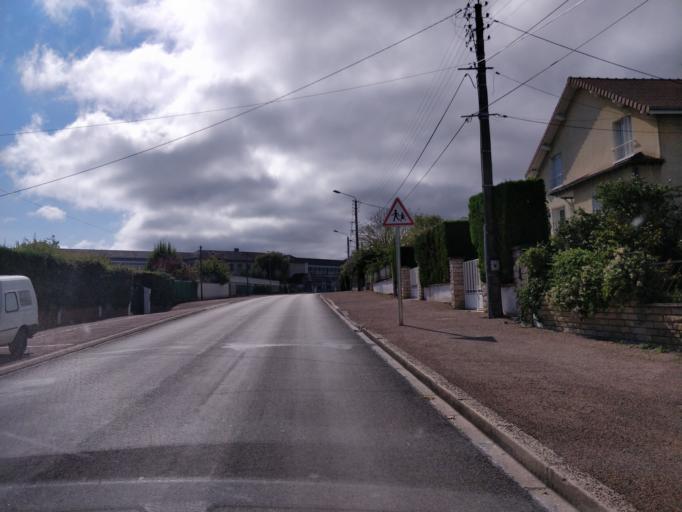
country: FR
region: Bourgogne
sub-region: Departement de l'Yonne
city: Saint-Florentin
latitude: 48.0024
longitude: 3.7268
